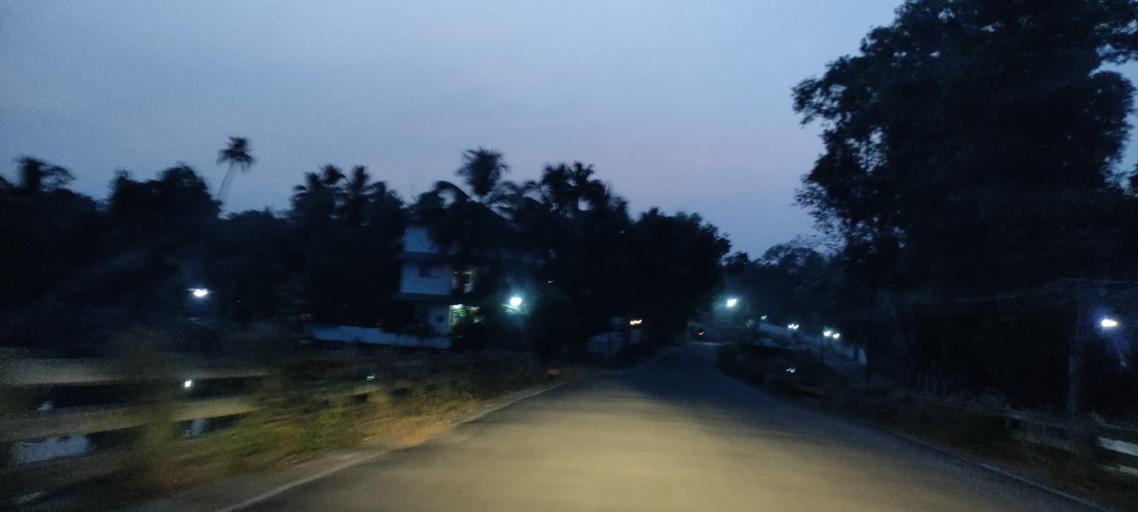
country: IN
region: Kerala
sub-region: Alappuzha
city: Mavelikara
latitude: 9.3202
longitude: 76.4342
